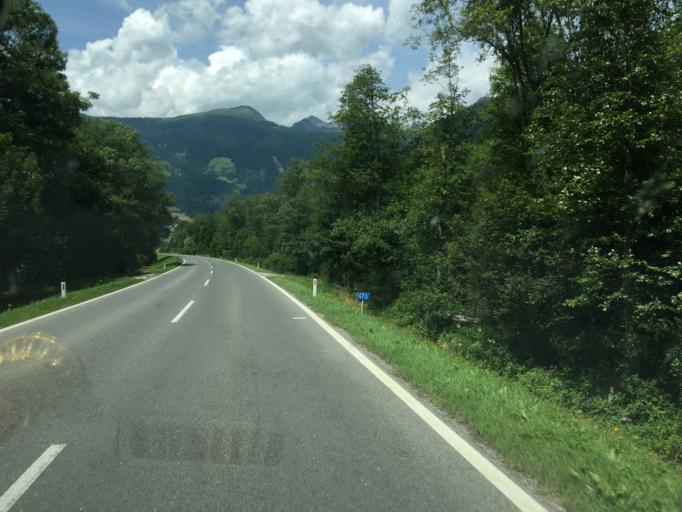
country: AT
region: Carinthia
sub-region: Politischer Bezirk Spittal an der Drau
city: Winklern
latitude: 46.8577
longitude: 12.9050
